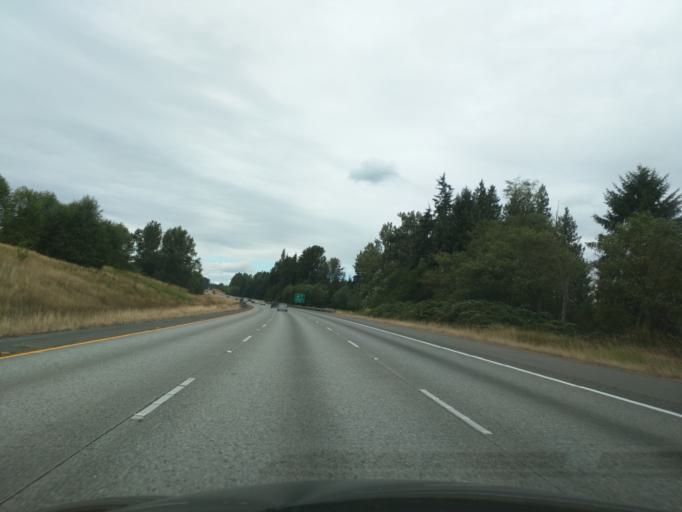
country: US
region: Washington
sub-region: Snohomish County
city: Bryant
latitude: 48.2239
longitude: -122.2225
